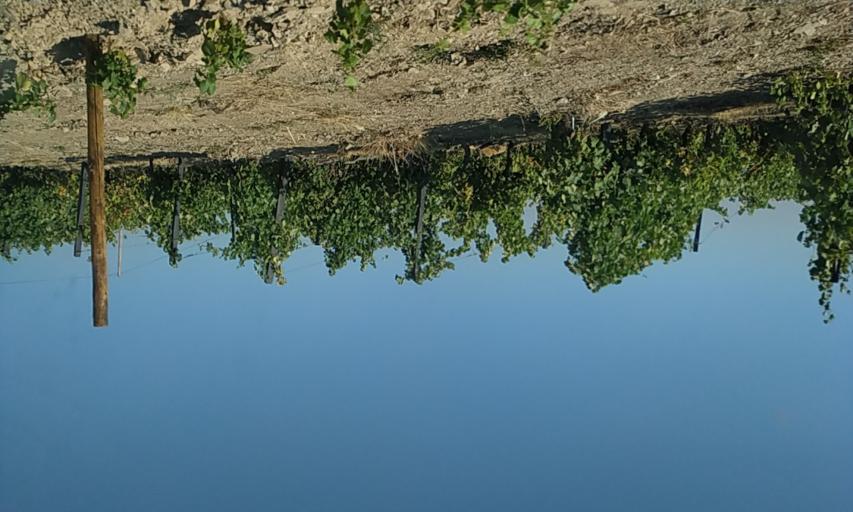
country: PT
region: Viseu
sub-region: Sao Joao da Pesqueira
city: Sao Joao da Pesqueira
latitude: 41.1649
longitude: -7.4124
